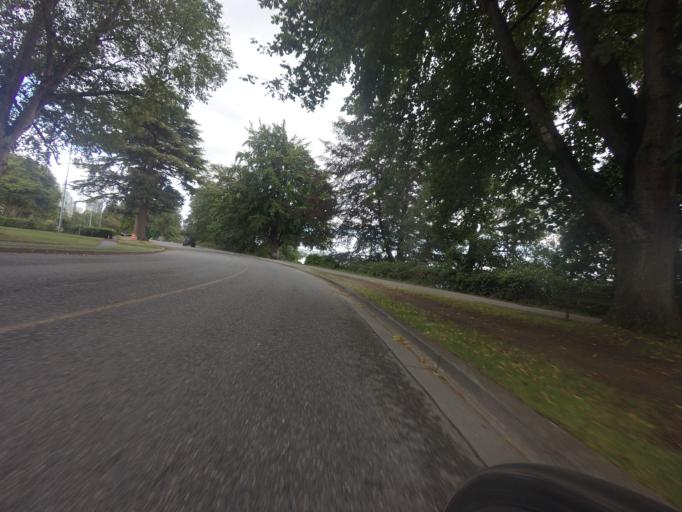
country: CA
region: British Columbia
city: West End
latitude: 49.2918
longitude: -123.1483
